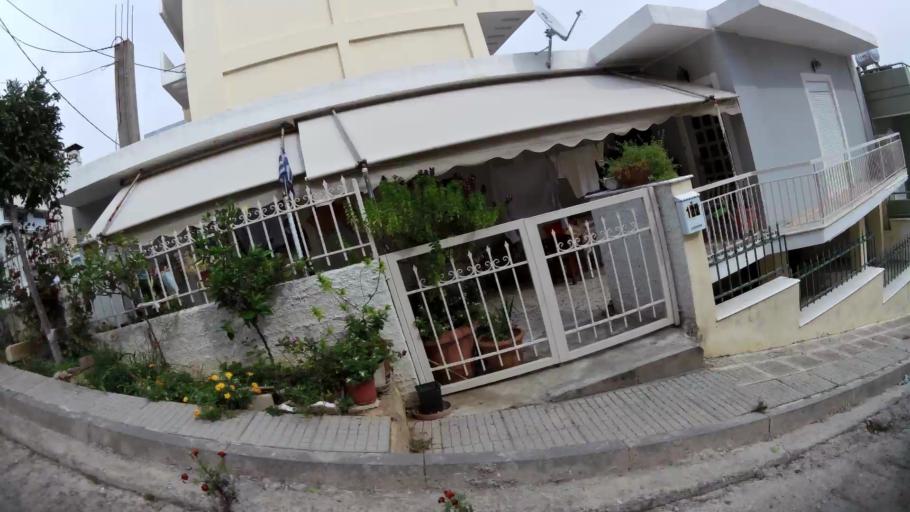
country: GR
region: Attica
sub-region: Nomarchia Athinas
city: Chaidari
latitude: 38.0216
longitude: 23.6469
